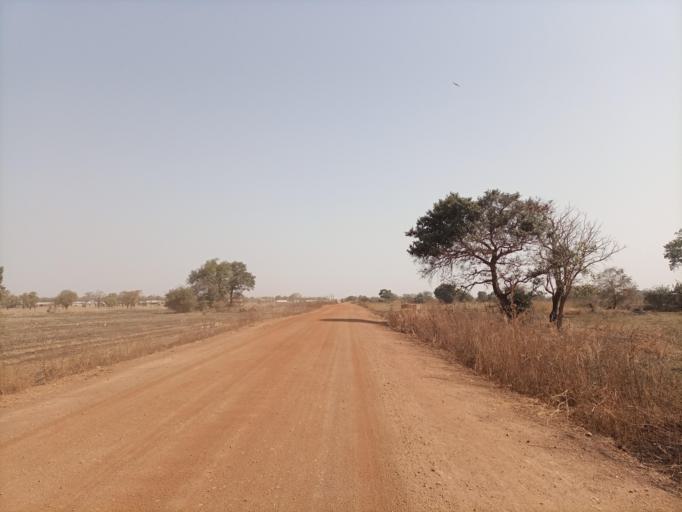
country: GH
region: Northern
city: Savelugu
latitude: 9.8122
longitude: -0.7748
